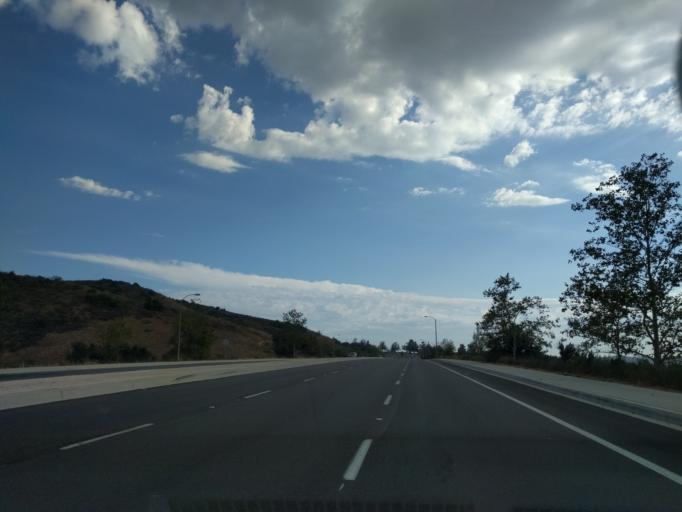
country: US
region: California
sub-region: Orange County
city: Las Flores
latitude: 33.5800
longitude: -117.6317
